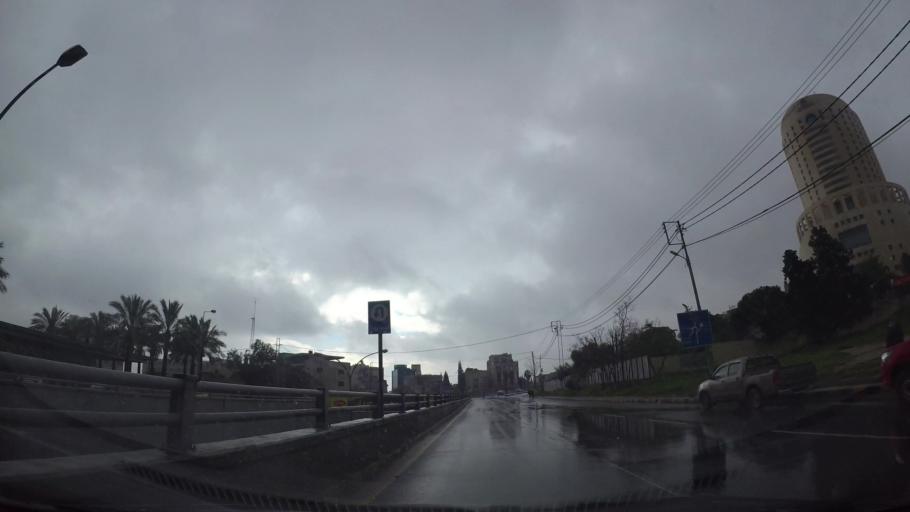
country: JO
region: Amman
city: Amman
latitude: 31.9551
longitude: 35.9096
